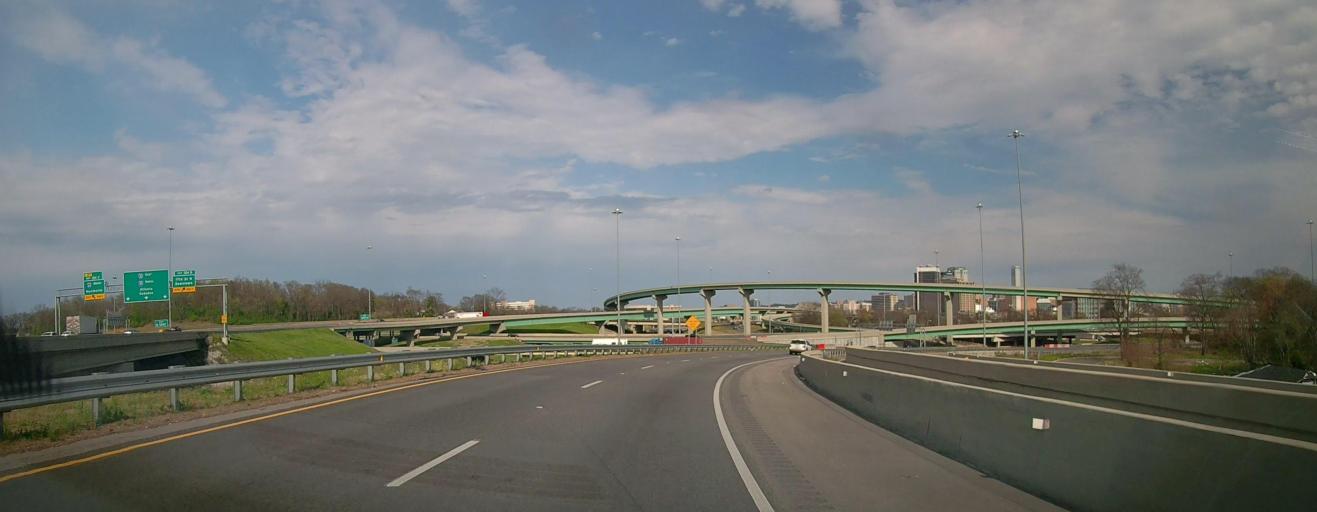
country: US
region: Alabama
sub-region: Jefferson County
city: Birmingham
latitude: 33.5203
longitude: -86.8292
